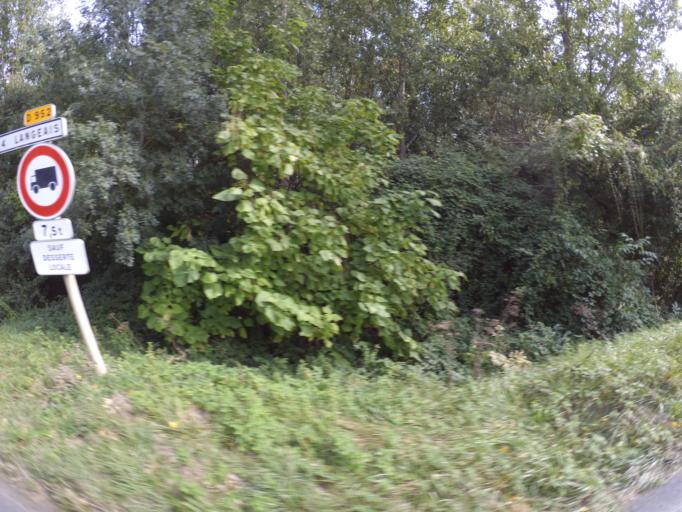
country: FR
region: Centre
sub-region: Departement d'Indre-et-Loire
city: Langeais
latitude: 47.3094
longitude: 0.3631
